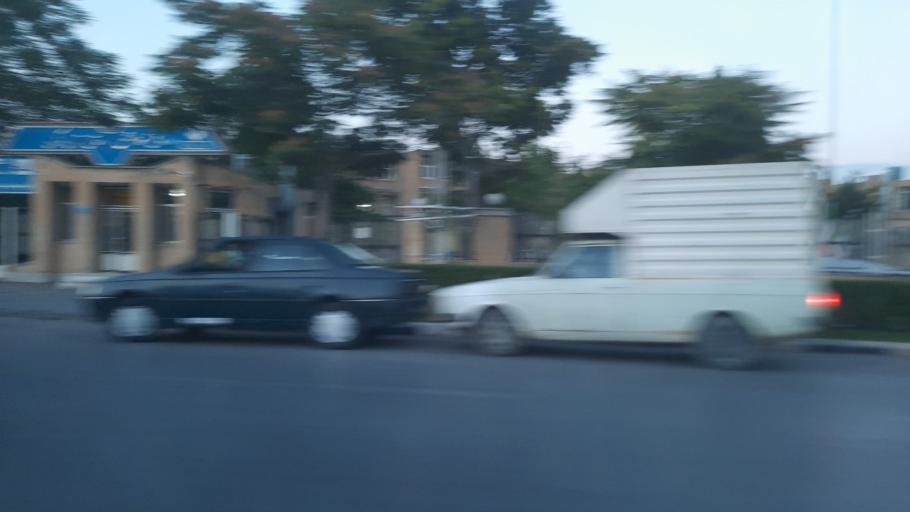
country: IR
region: Markazi
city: Arak
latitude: 34.0752
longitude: 49.7029
